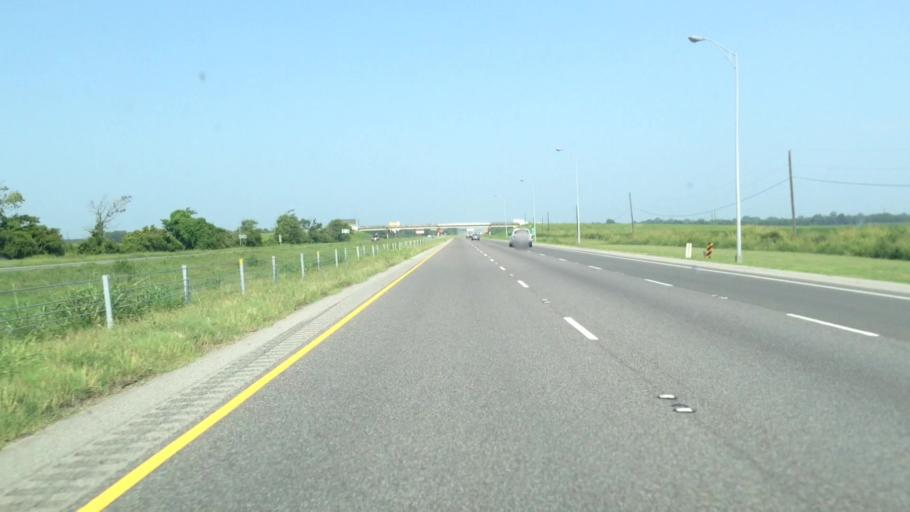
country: US
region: Mississippi
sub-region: Warren County
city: Vicksburg
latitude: 32.3253
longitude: -90.9950
